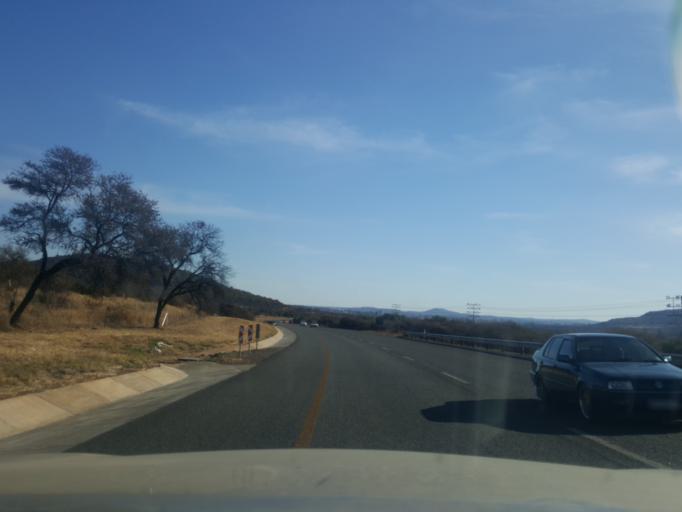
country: ZA
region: North-West
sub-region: Ngaka Modiri Molema District Municipality
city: Zeerust
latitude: -25.5381
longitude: 26.1257
